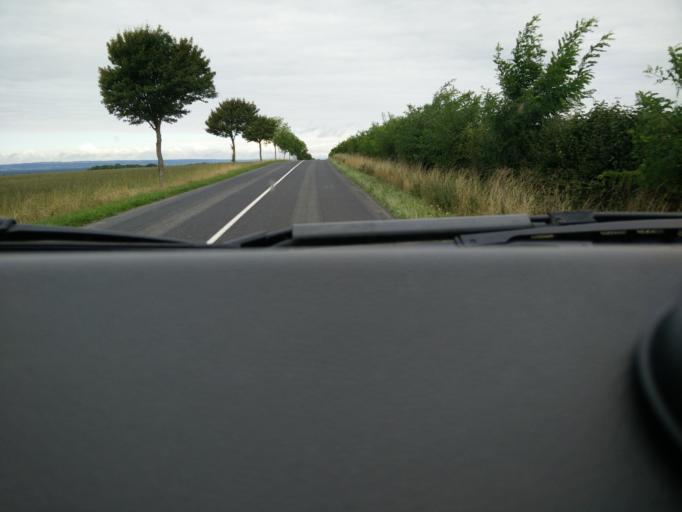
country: FR
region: Lorraine
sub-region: Departement de Meurthe-et-Moselle
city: Montauville
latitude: 48.9313
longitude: 5.8985
